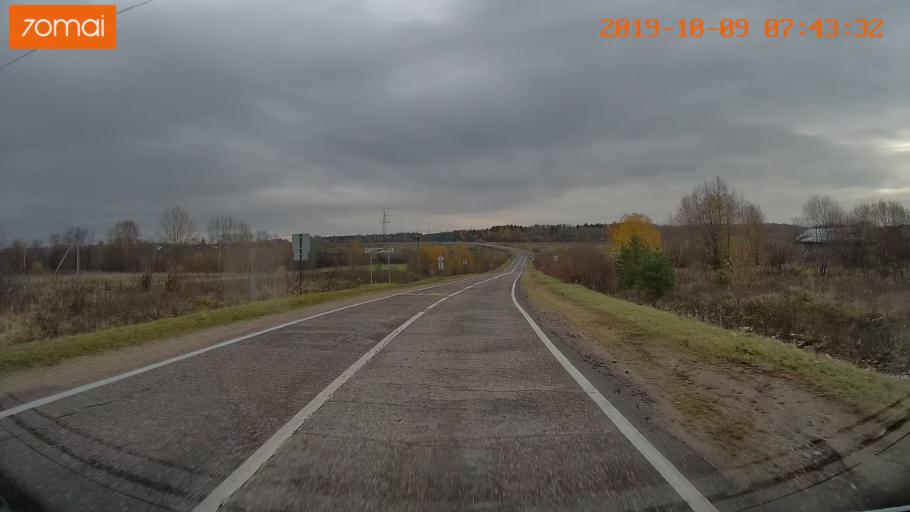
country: RU
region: Jaroslavl
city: Kukoboy
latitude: 58.6454
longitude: 39.7368
